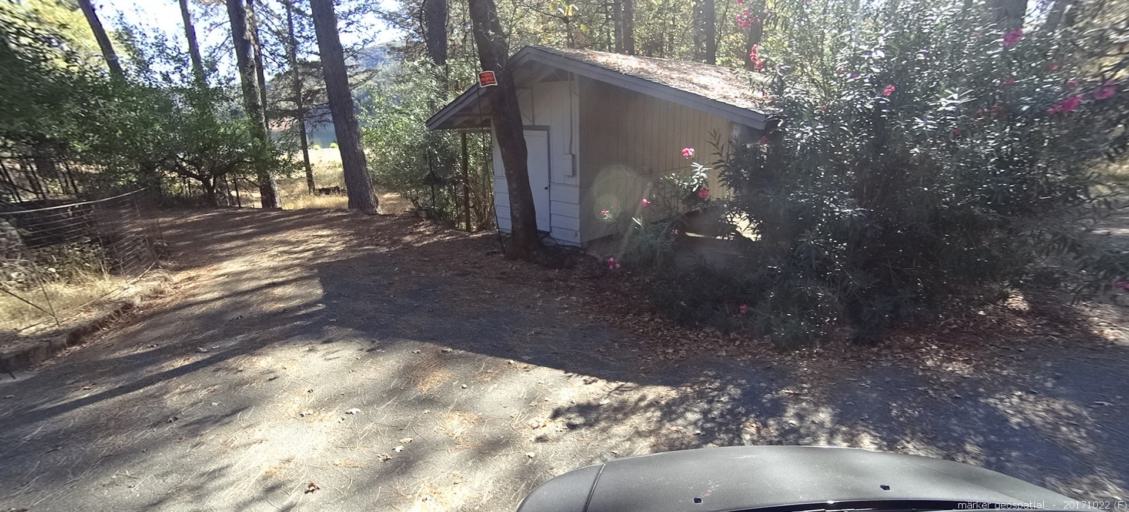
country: US
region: California
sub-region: Shasta County
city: Central Valley (historical)
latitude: 40.8574
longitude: -122.3968
